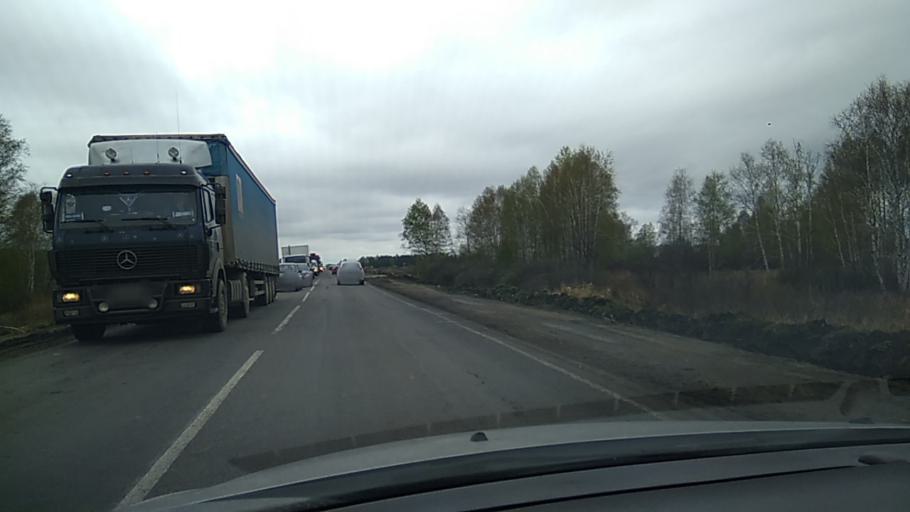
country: RU
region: Kurgan
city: Shadrinsk
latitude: 56.1541
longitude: 63.4067
